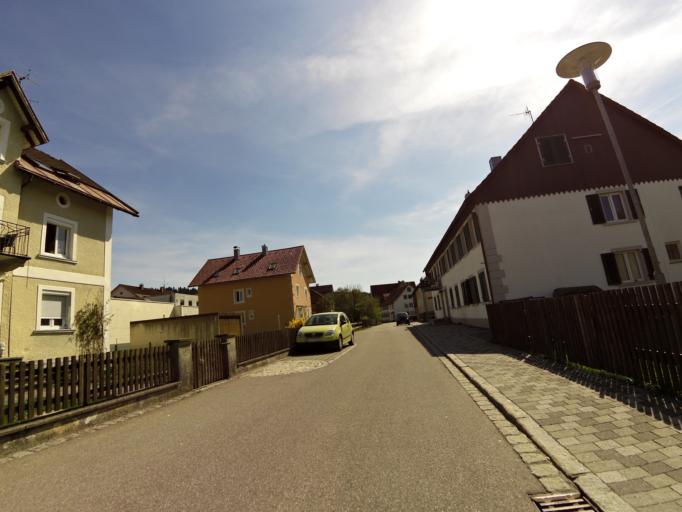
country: DE
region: Bavaria
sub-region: Swabia
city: Weiler-Simmerberg
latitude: 47.5837
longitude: 9.9147
